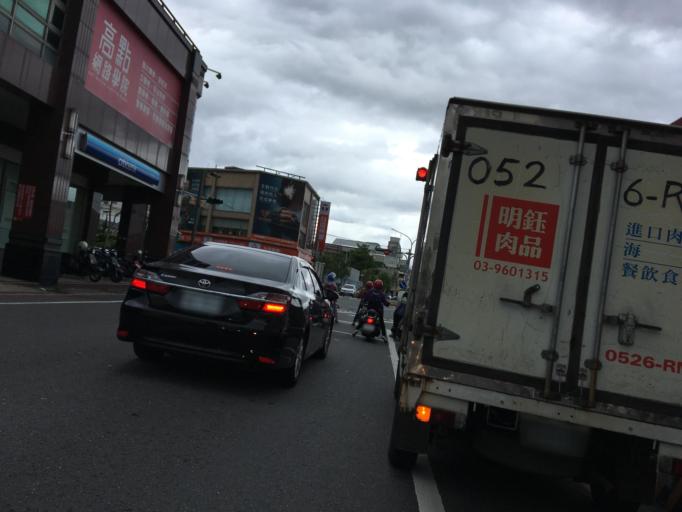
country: TW
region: Taiwan
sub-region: Yilan
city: Yilan
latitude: 24.6801
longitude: 121.7717
